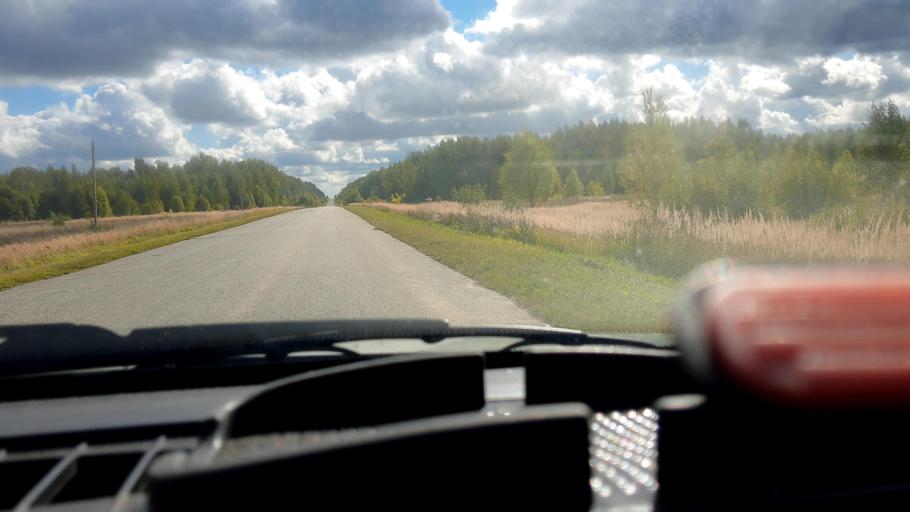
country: RU
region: Mariy-El
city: Kilemary
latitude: 56.9323
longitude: 46.6998
